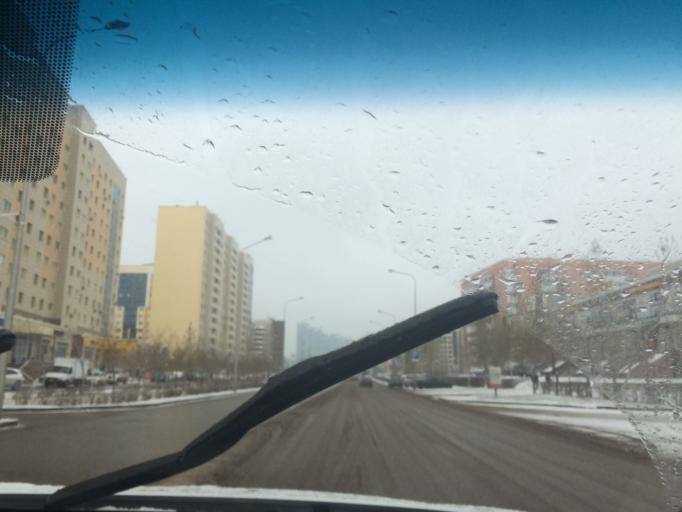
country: KZ
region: Astana Qalasy
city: Astana
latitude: 51.1213
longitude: 71.4211
